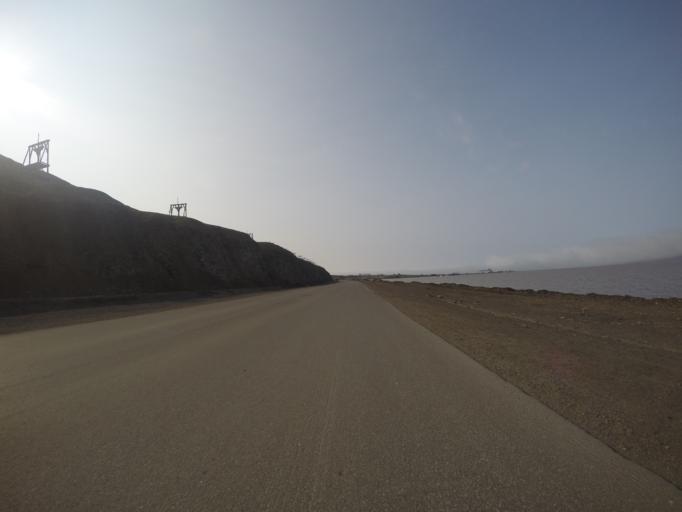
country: SJ
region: Svalbard
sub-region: Spitsbergen
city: Longyearbyen
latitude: 78.2330
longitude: 15.5654
